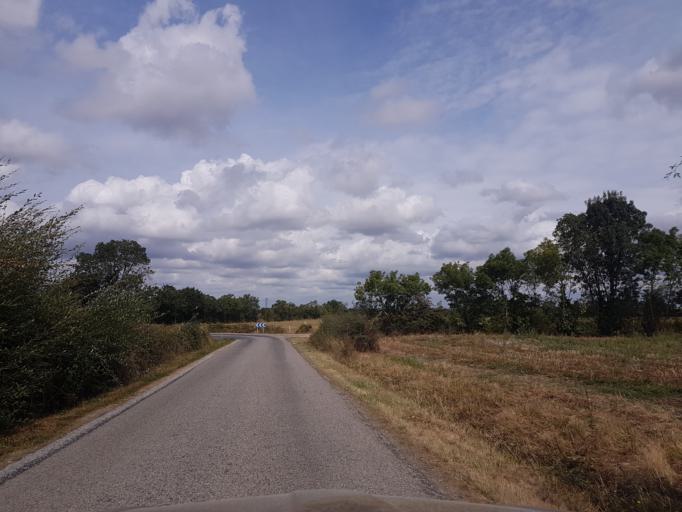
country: FR
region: Pays de la Loire
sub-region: Departement de la Loire-Atlantique
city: Petit-Mars
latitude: 47.4094
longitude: -1.4311
